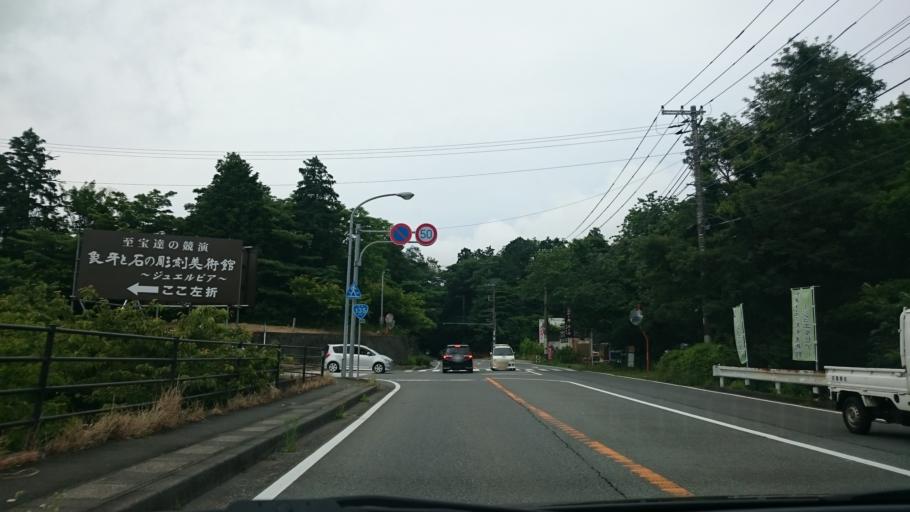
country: JP
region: Shizuoka
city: Ito
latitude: 34.9151
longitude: 139.1203
